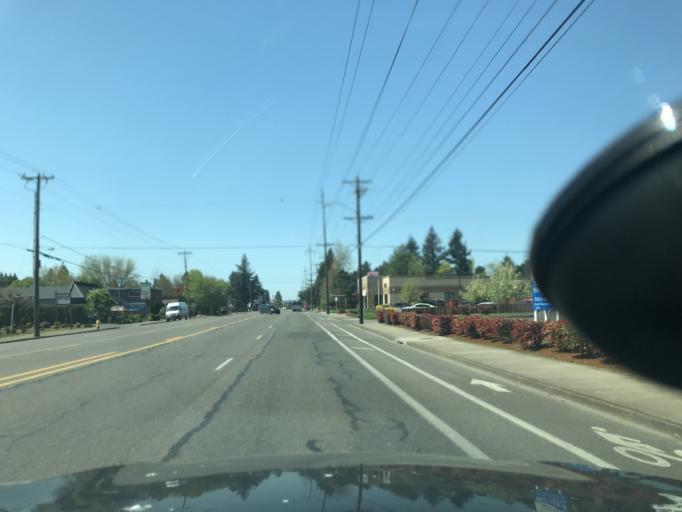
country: US
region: Oregon
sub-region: Multnomah County
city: Gresham
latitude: 45.5046
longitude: -122.4766
